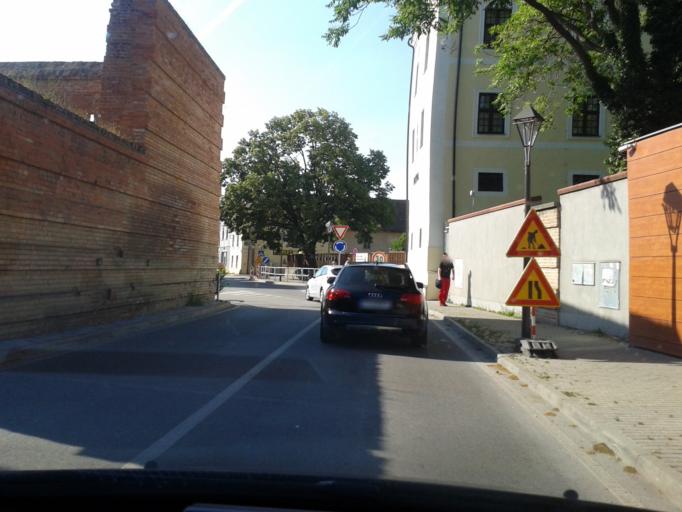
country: SK
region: Trnavsky
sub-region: Okres Trnava
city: Trnava
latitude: 48.3748
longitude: 17.5927
